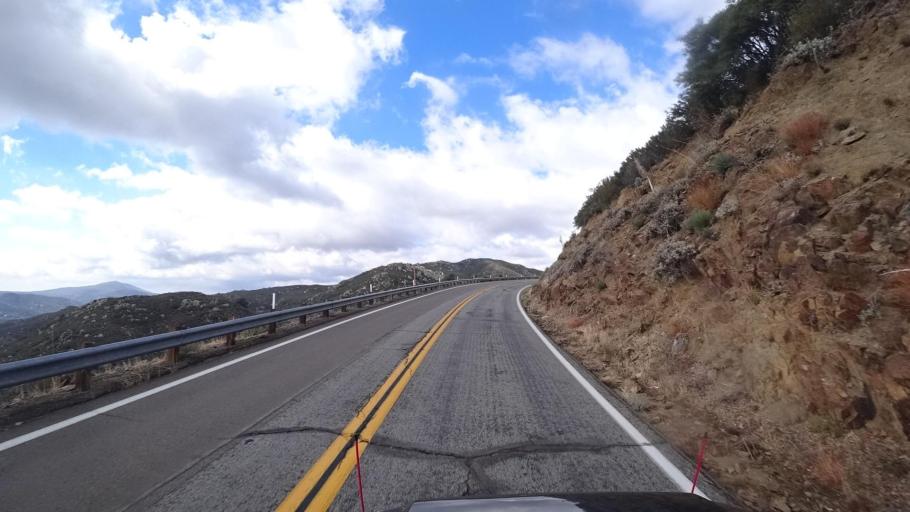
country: US
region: California
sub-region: San Diego County
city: Pine Valley
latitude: 32.8296
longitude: -116.4958
